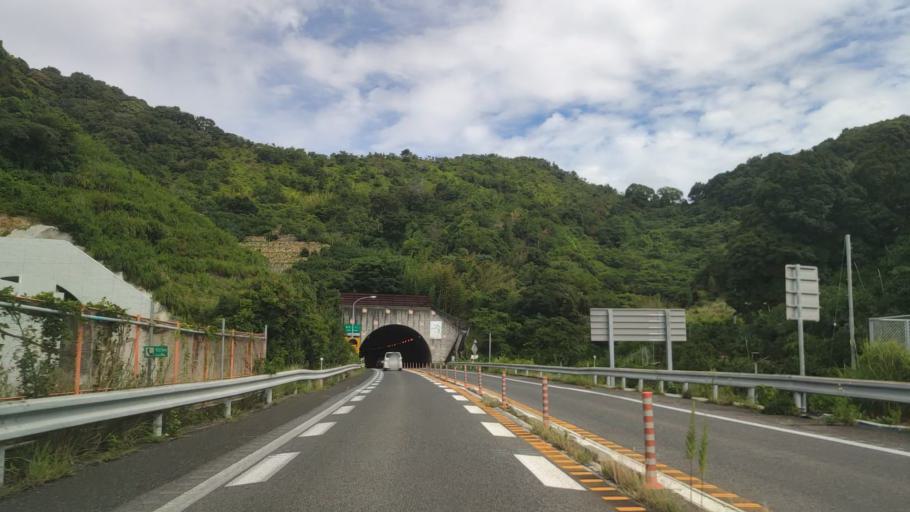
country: JP
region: Wakayama
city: Kainan
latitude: 34.0213
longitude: 135.1980
